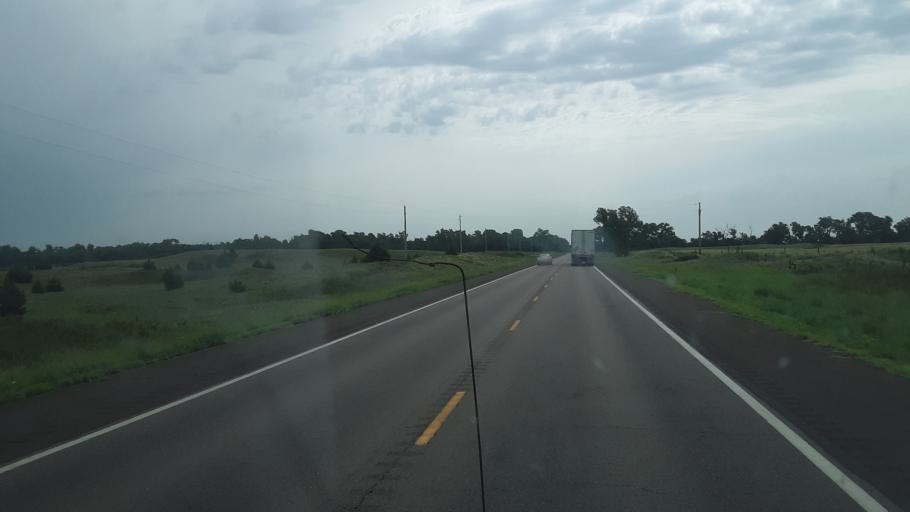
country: US
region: Kansas
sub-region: Stafford County
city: Saint John
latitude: 37.9558
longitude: -98.7261
